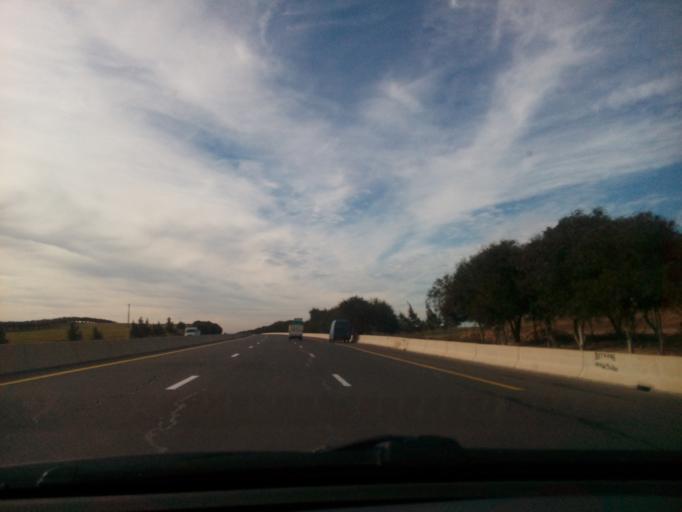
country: DZ
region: Sidi Bel Abbes
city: Sidi Bel Abbes
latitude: 35.2150
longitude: -0.6811
